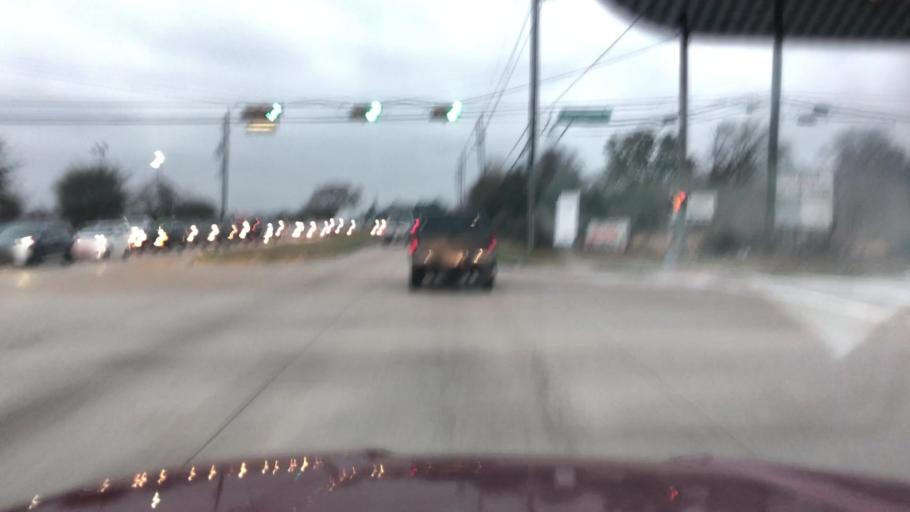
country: US
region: Texas
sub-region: Harris County
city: Tomball
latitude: 30.0458
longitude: -95.5384
